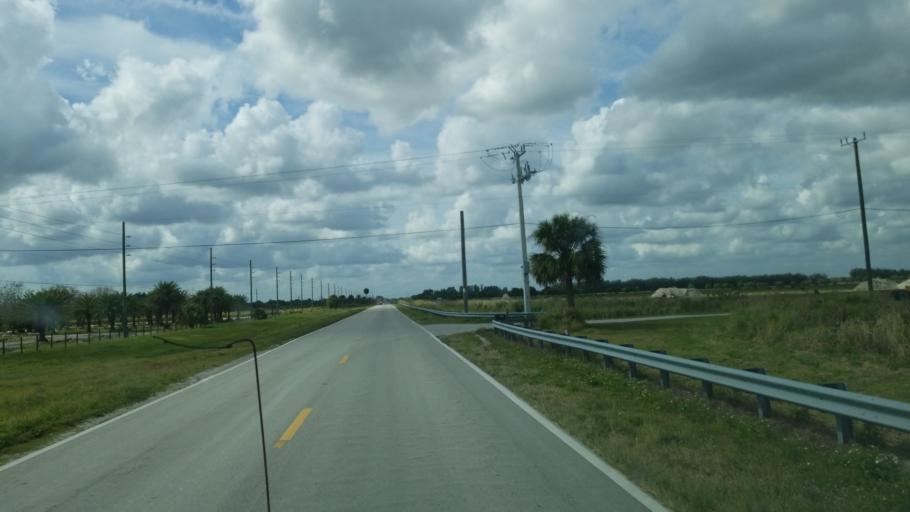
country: US
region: Florida
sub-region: Saint Lucie County
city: Lakewood Park
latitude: 27.4476
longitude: -80.5175
